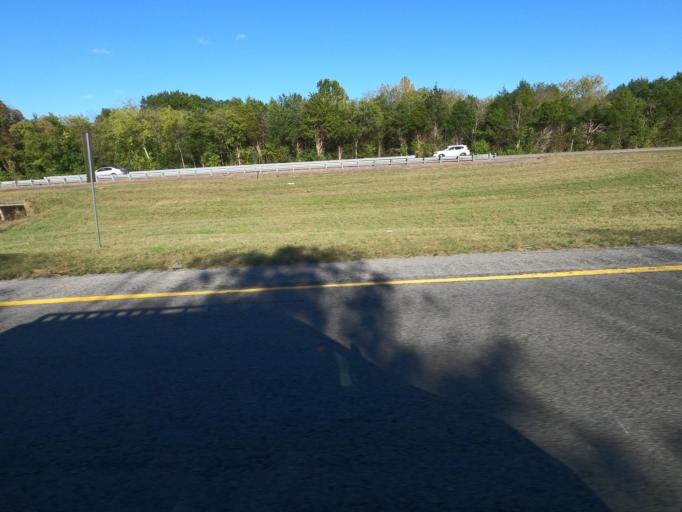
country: US
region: Tennessee
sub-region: Rutherford County
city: Plainview
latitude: 35.6729
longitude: -86.2830
